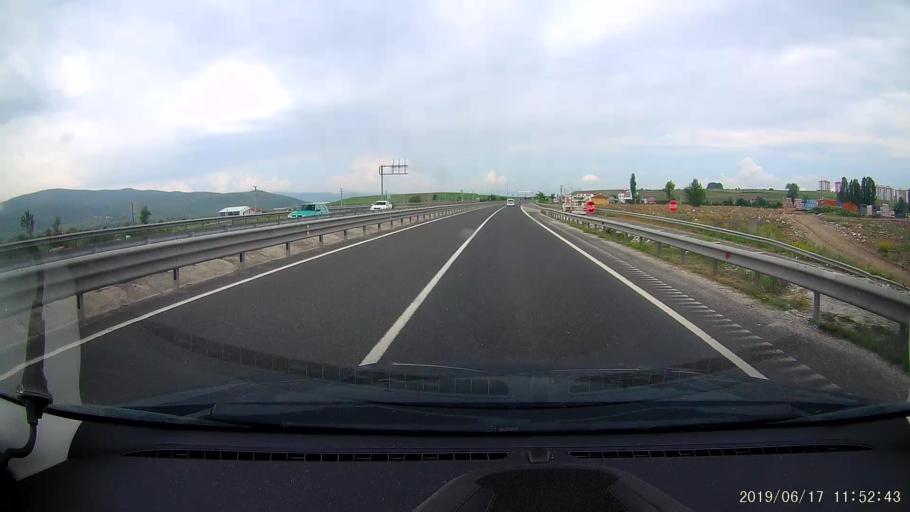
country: TR
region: Cankiri
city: Atkaracalar
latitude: 40.8073
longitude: 33.0775
